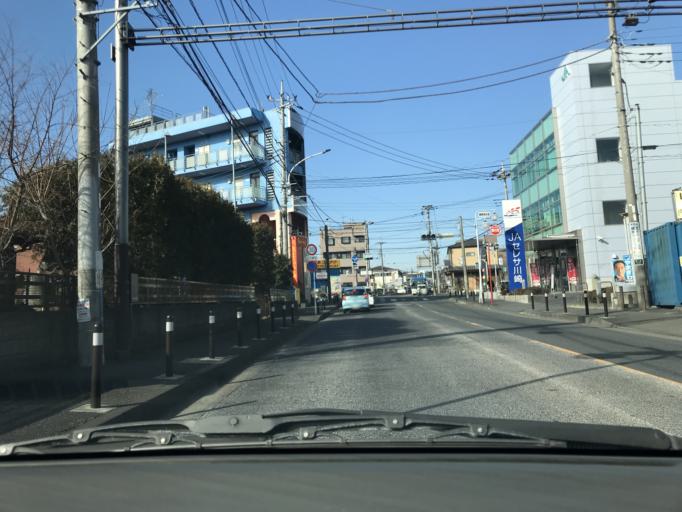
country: JP
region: Tokyo
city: Chofugaoka
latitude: 35.5957
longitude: 139.5559
